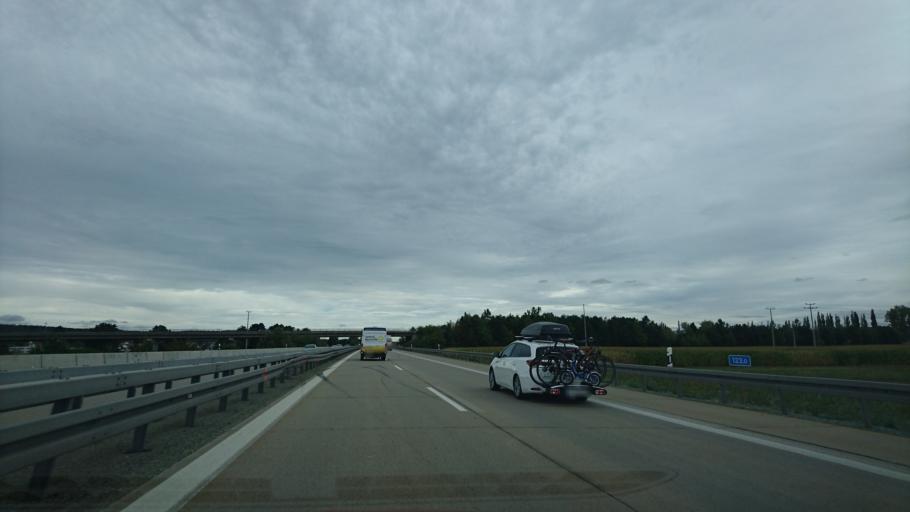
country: DE
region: Bavaria
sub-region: Upper Palatinate
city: Pirk
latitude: 49.6302
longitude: 12.1487
